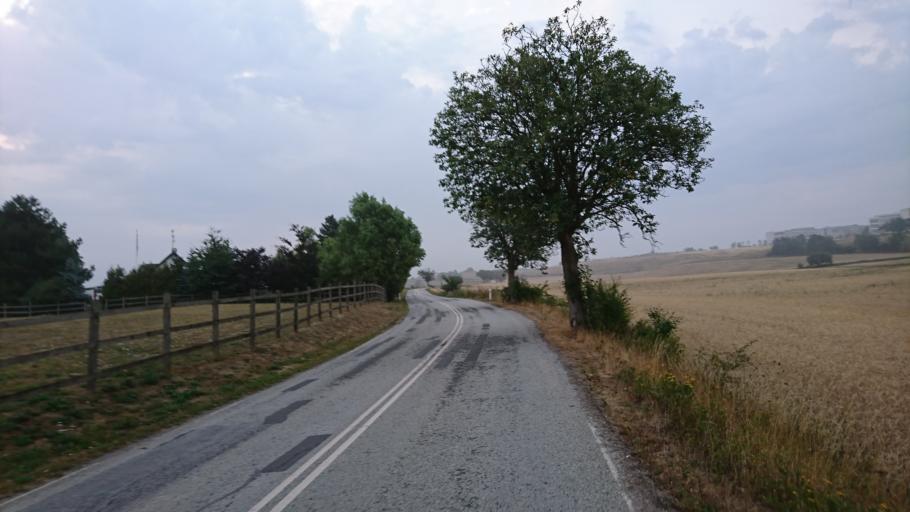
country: DK
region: Capital Region
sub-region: Egedal Kommune
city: Smorumnedre
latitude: 55.7596
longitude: 12.2978
